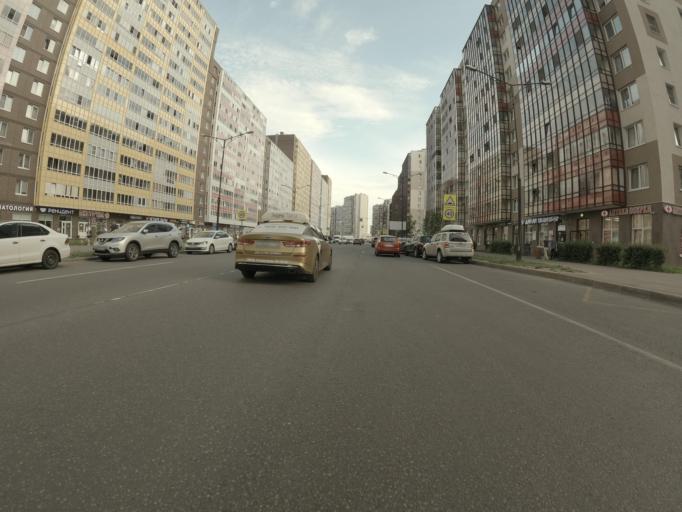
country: RU
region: Leningrad
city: Rybatskoye
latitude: 59.9020
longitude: 30.5122
